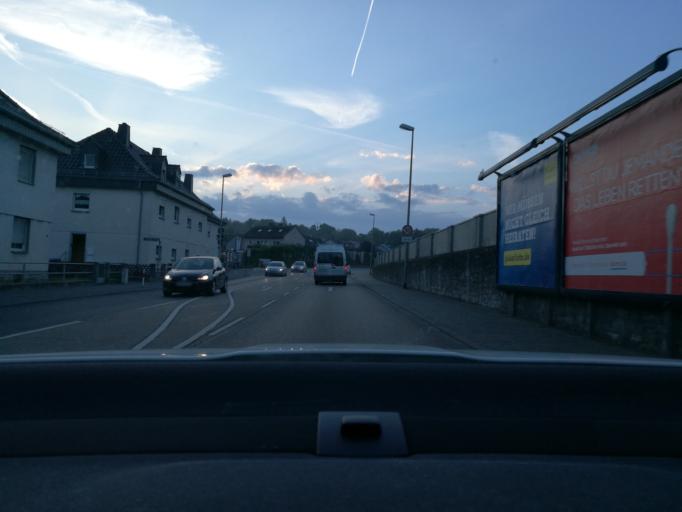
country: DE
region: Hesse
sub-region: Regierungsbezirk Giessen
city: Limburg an der Lahn
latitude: 50.3820
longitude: 8.0734
